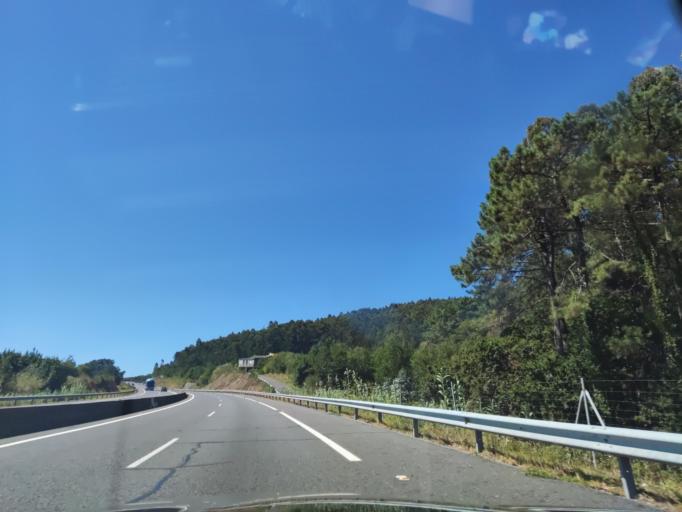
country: ES
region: Galicia
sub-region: Provincia da Coruna
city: Boiro
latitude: 42.6543
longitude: -8.9005
